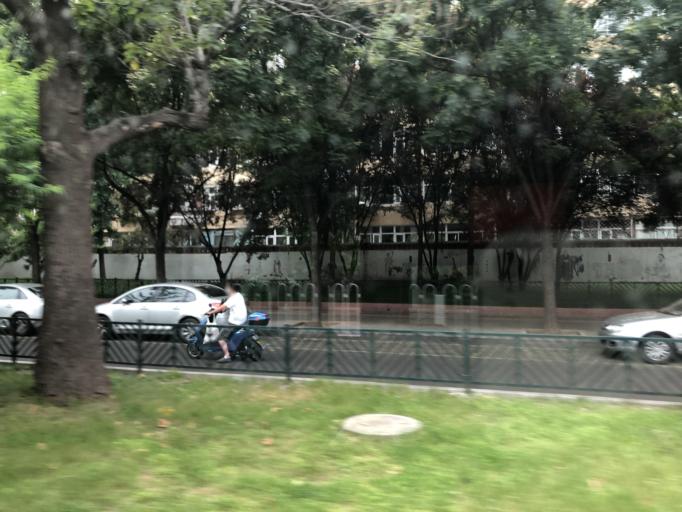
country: CN
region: Beijing
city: Jinrongjie
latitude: 39.9313
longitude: 116.3114
